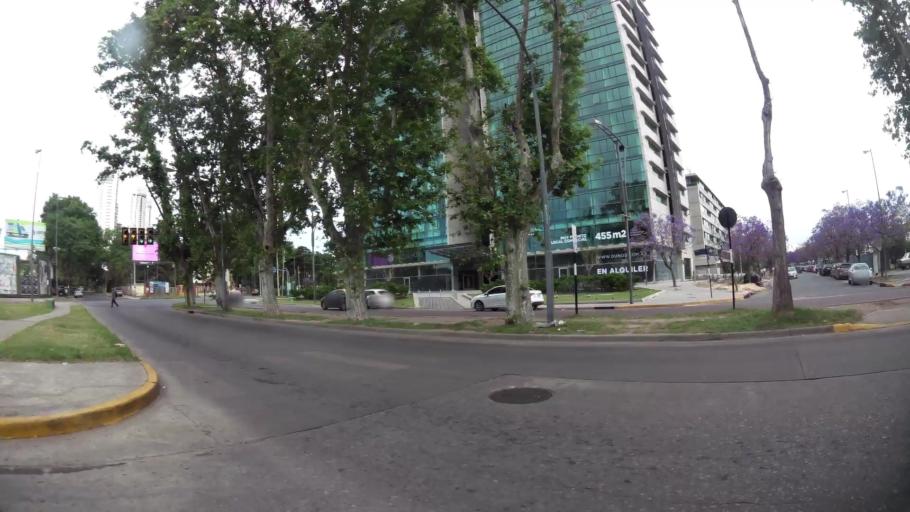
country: AR
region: Santa Fe
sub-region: Departamento de Rosario
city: Rosario
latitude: -32.9263
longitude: -60.6659
